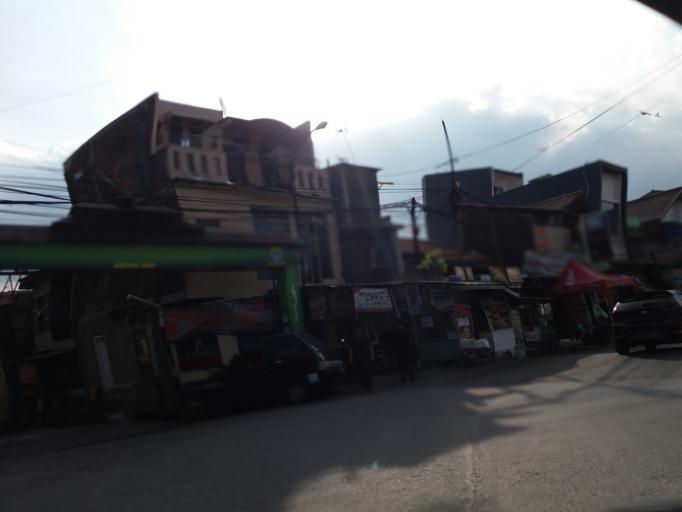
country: ID
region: West Java
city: Bandung
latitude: -6.9517
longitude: 107.6264
